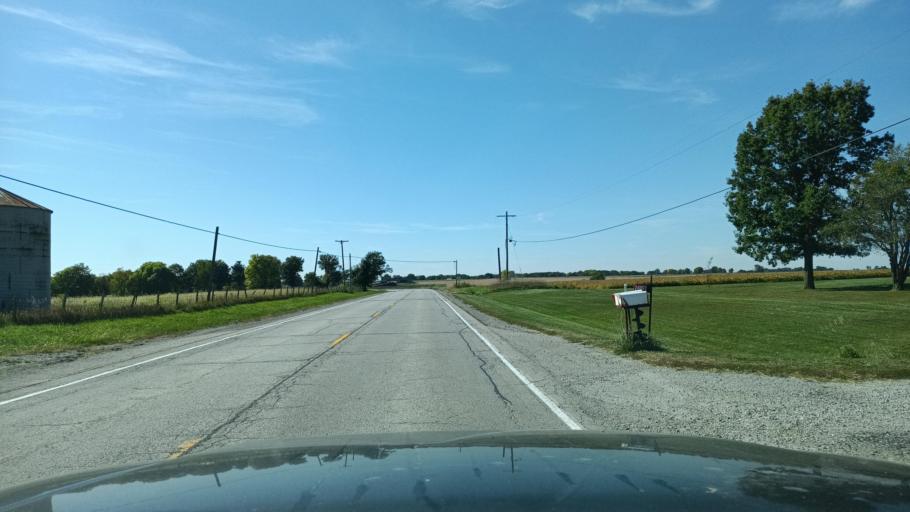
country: US
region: Illinois
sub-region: De Witt County
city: Farmer City
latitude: 40.2321
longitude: -88.6719
